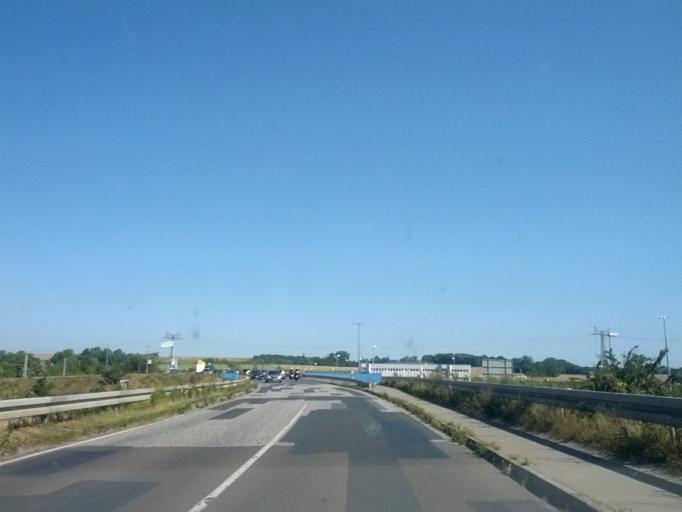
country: DE
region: Mecklenburg-Vorpommern
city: Sagard
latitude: 54.4887
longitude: 13.5783
